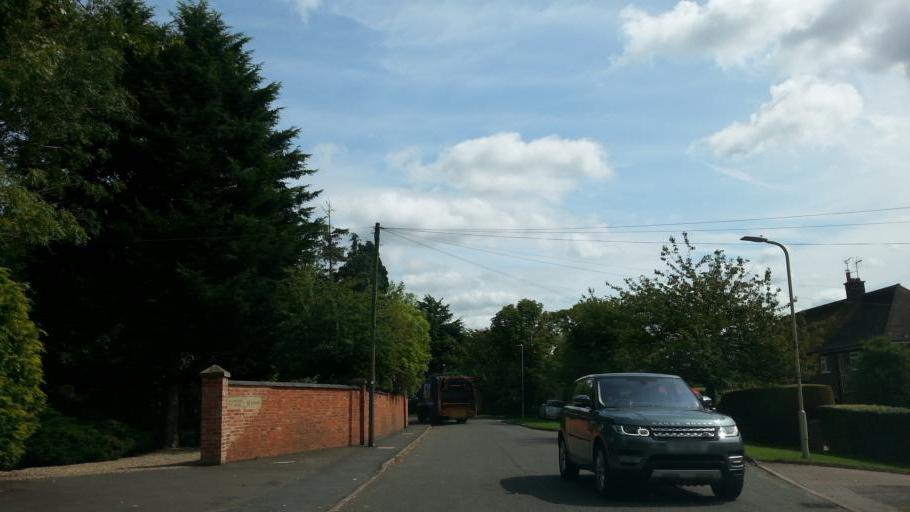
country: GB
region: England
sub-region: Leicestershire
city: Kibworth Harcourt
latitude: 52.5277
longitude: -1.0020
